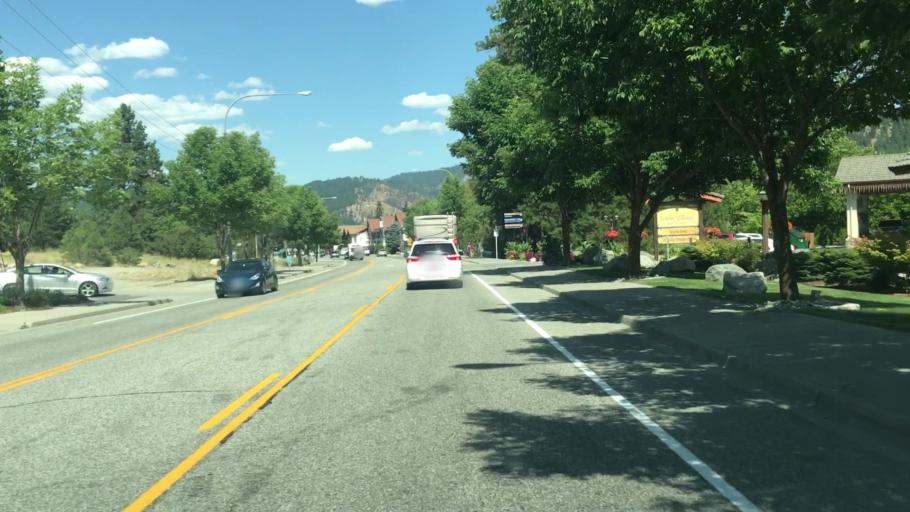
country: US
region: Washington
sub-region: Chelan County
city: Leavenworth
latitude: 47.5892
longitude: -120.6736
